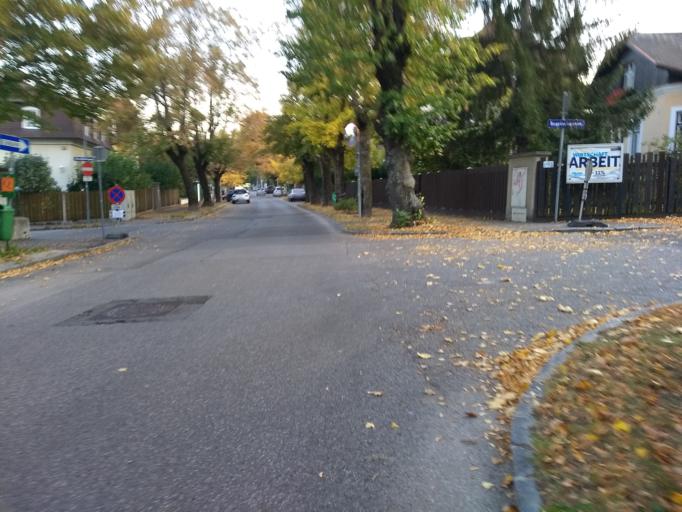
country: AT
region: Lower Austria
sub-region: Politischer Bezirk Modling
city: Perchtoldsdorf
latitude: 48.1240
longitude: 16.2583
